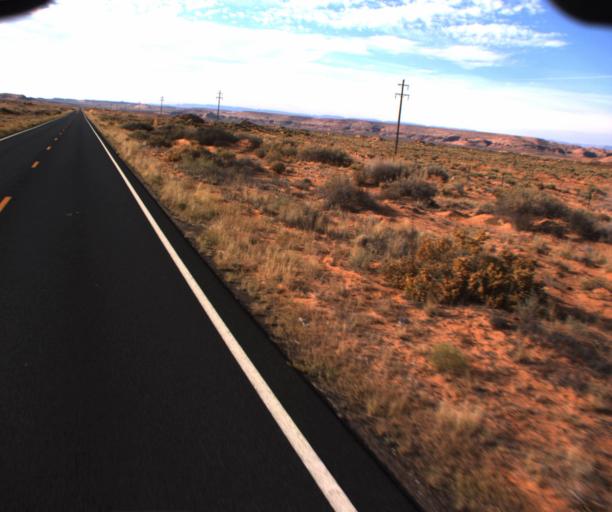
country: US
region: Arizona
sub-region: Apache County
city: Many Farms
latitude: 36.8188
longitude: -109.6457
